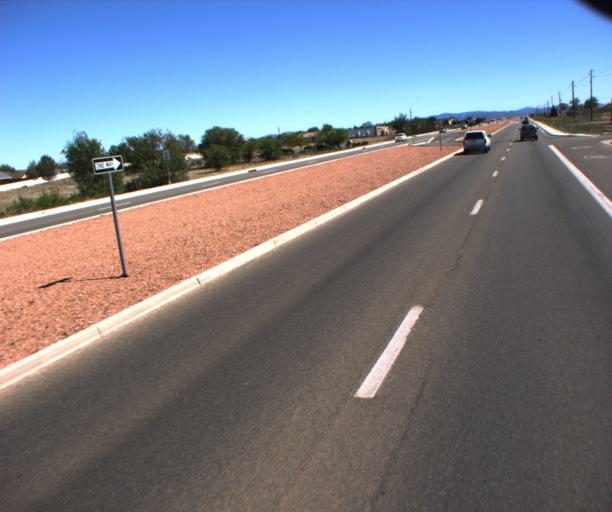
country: US
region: Arizona
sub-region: Yavapai County
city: Chino Valley
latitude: 34.7280
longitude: -112.4541
